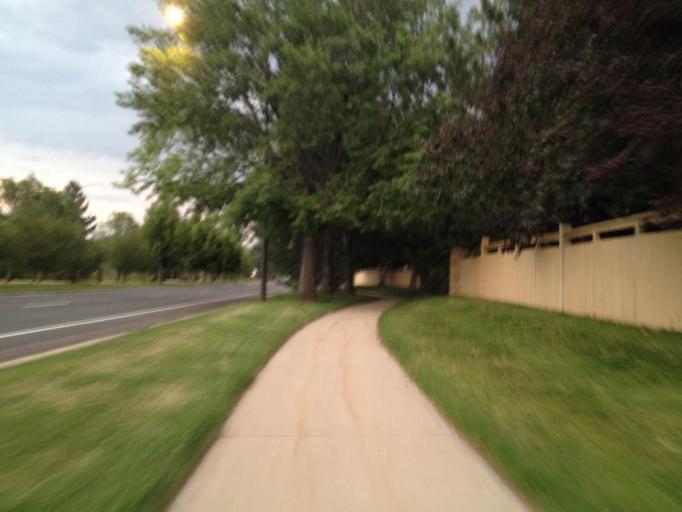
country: US
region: Colorado
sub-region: Boulder County
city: Superior
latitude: 39.9650
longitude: -105.1517
